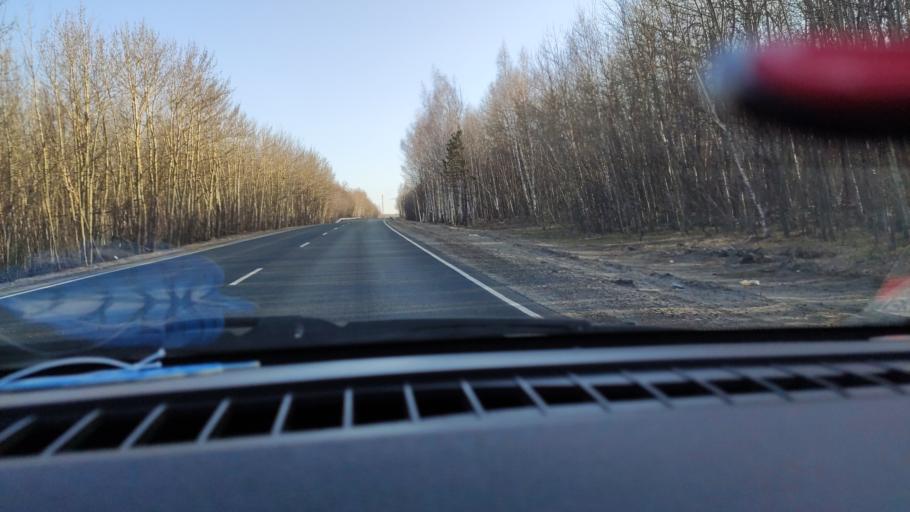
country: RU
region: Saratov
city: Khvalynsk
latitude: 52.4498
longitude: 48.0116
